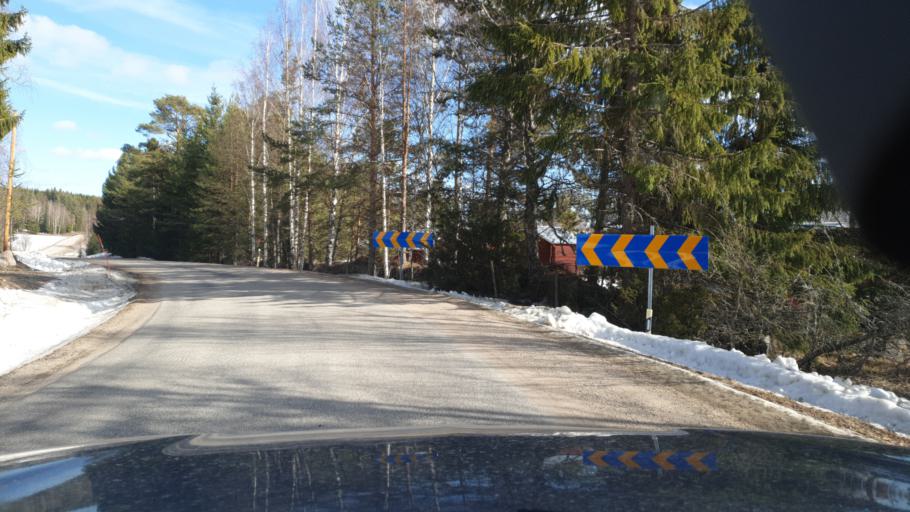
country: SE
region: Gaevleborg
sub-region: Ljusdals Kommun
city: Ljusdal
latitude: 61.8460
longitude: 15.9708
